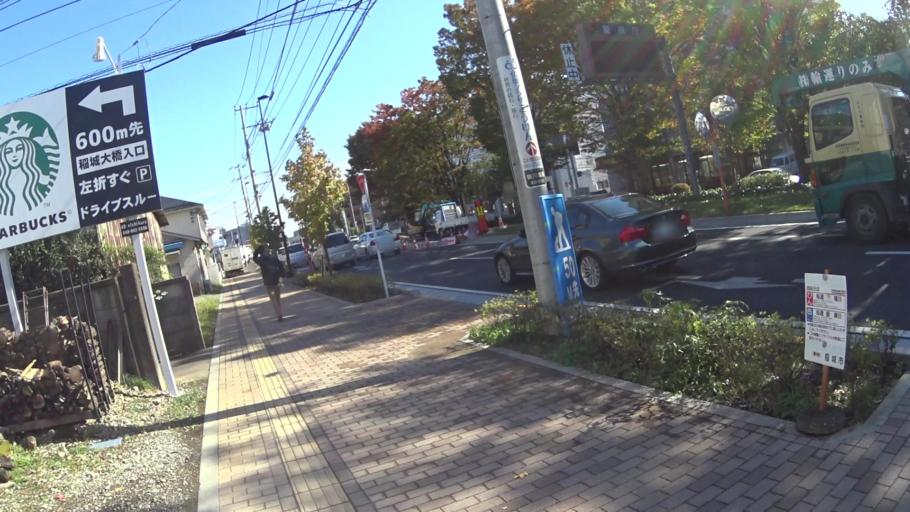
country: JP
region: Tokyo
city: Chofugaoka
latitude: 35.6391
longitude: 139.5014
